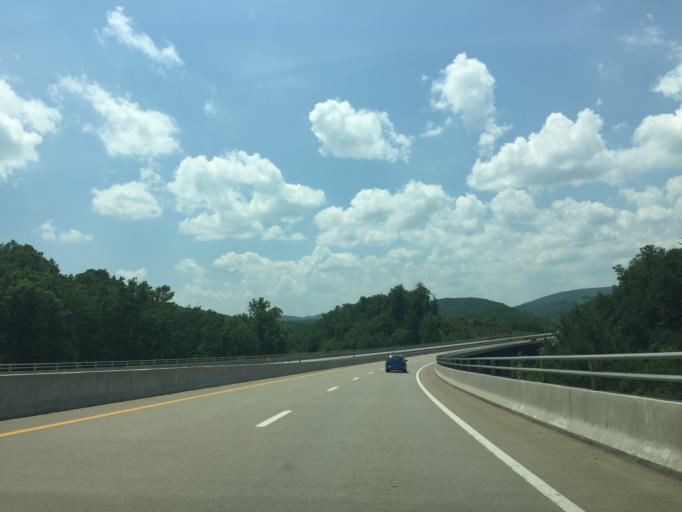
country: US
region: Virginia
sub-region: Shenandoah County
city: Woodstock
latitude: 39.0673
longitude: -78.6526
